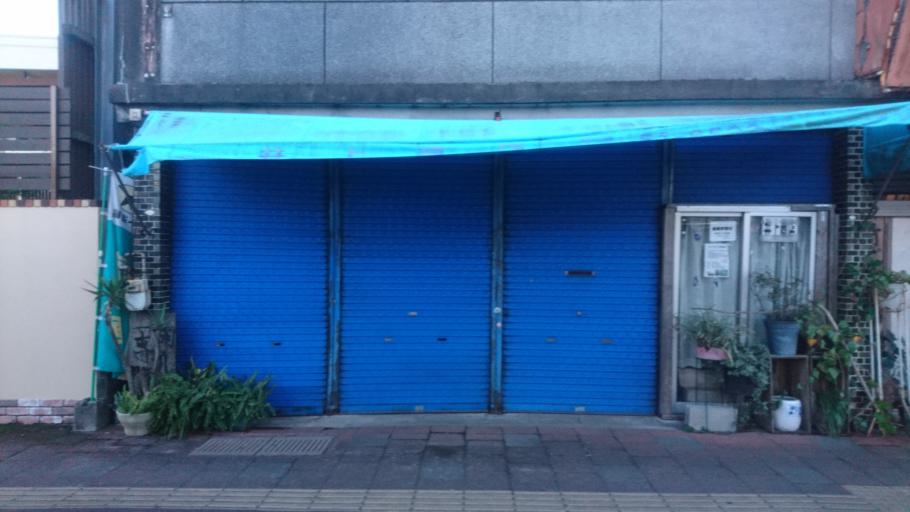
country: JP
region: Miyazaki
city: Miyazaki-shi
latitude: 31.8962
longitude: 131.4208
